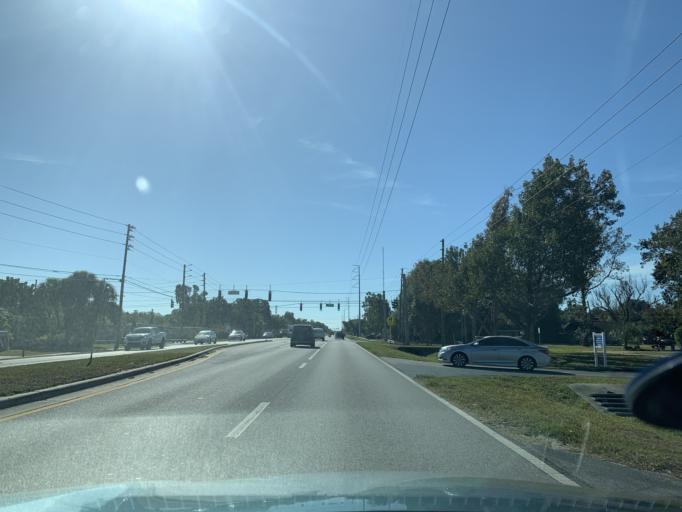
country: US
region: Florida
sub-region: Pinellas County
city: Seminole
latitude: 27.8586
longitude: -82.7624
